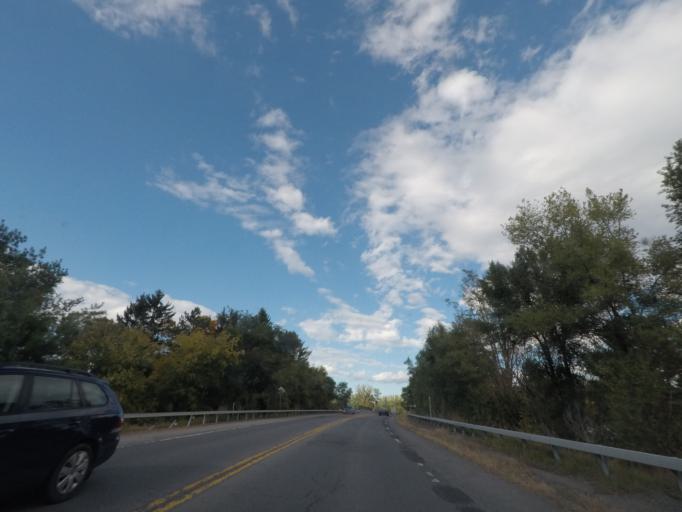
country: US
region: New York
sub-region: Schenectady County
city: Rotterdam
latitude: 42.7572
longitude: -73.9437
